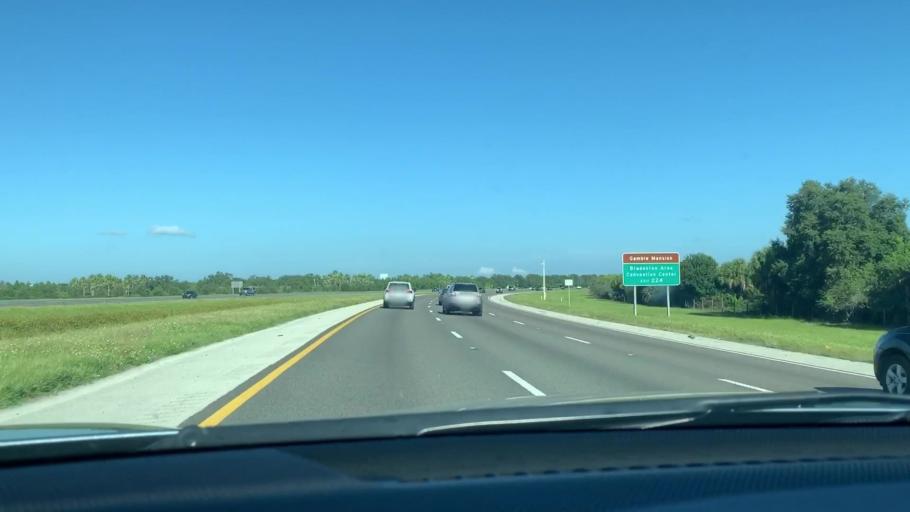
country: US
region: Florida
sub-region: Manatee County
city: Ellenton
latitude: 27.5106
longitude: -82.4982
